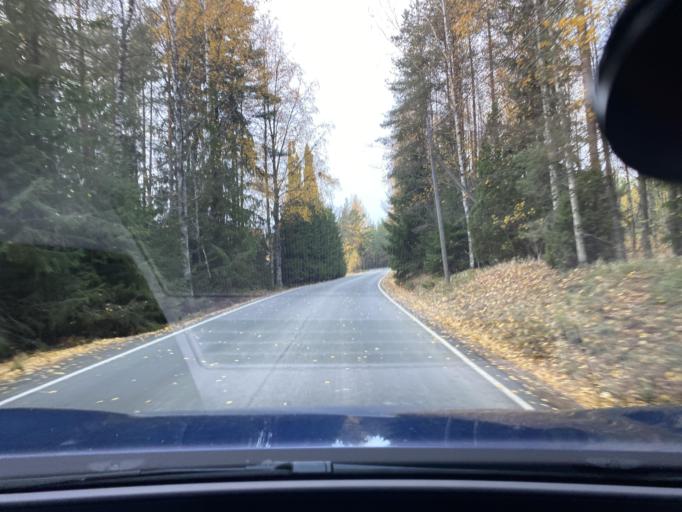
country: FI
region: Varsinais-Suomi
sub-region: Loimaa
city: Alastaro
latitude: 61.0993
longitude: 22.8935
